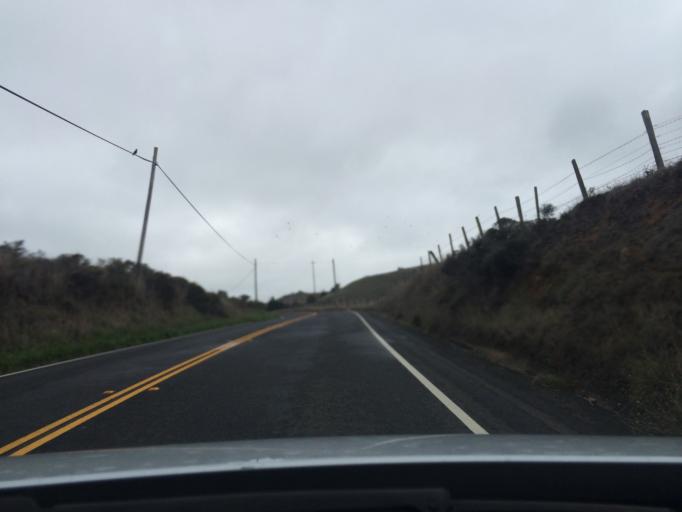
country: US
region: California
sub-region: Marin County
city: Inverness
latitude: 38.1738
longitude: -122.8996
